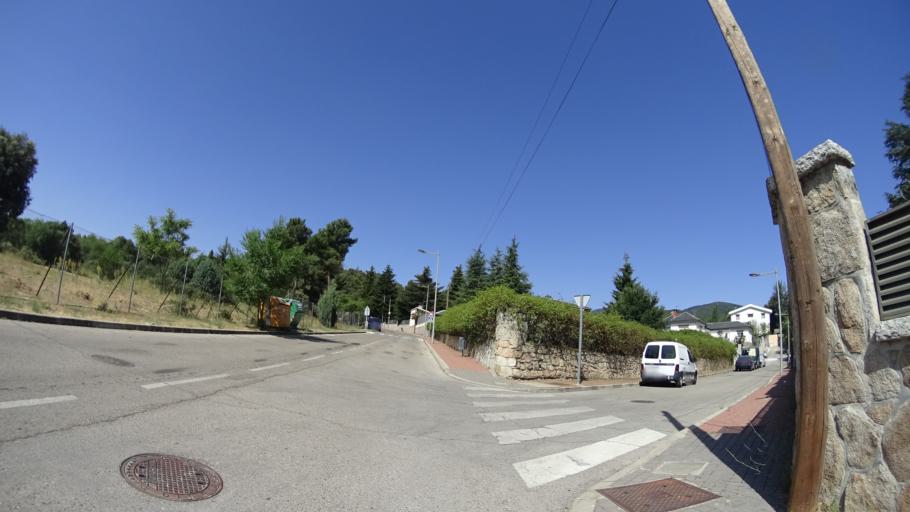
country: ES
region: Madrid
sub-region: Provincia de Madrid
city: Guadarrama
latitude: 40.6801
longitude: -4.1020
